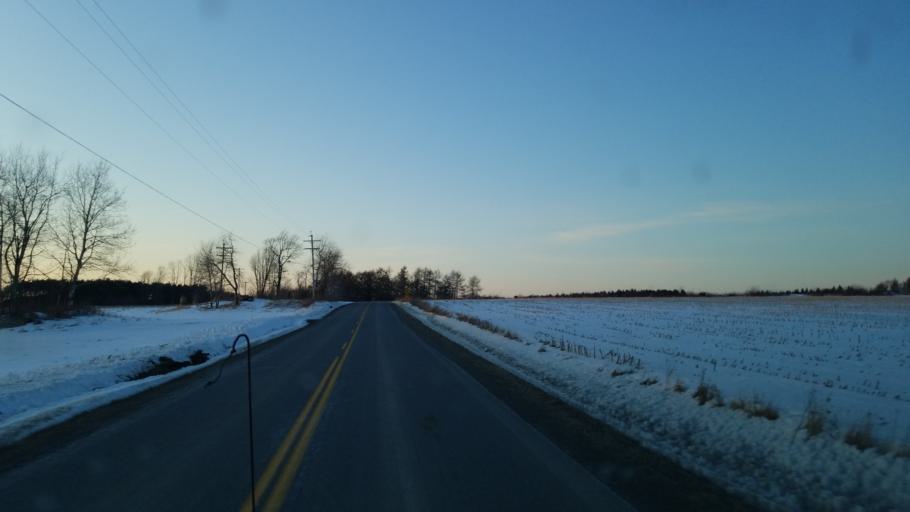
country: US
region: Pennsylvania
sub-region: Tioga County
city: Westfield
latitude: 42.0043
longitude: -77.6940
